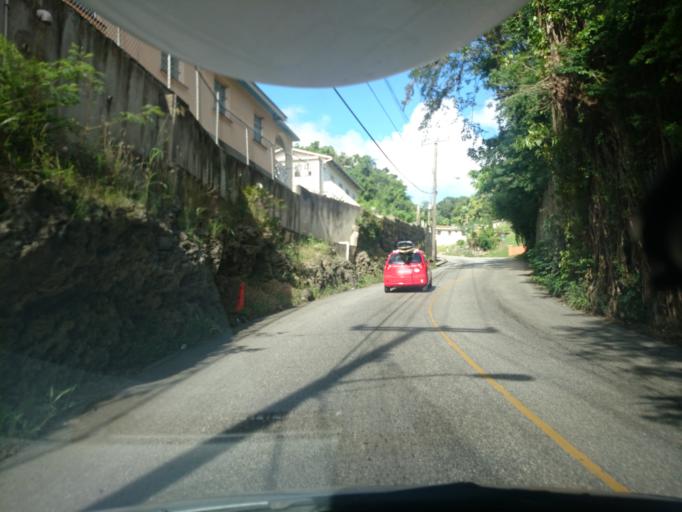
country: BB
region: Saint Thomas
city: Welchman Hall
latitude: 13.1429
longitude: -59.5546
